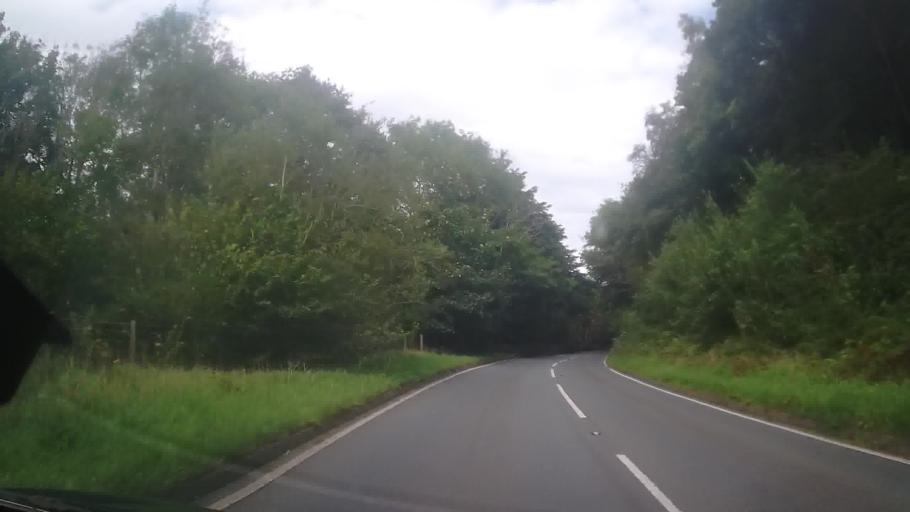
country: GB
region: Wales
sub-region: Gwynedd
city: Barmouth
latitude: 52.7233
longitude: -3.9907
